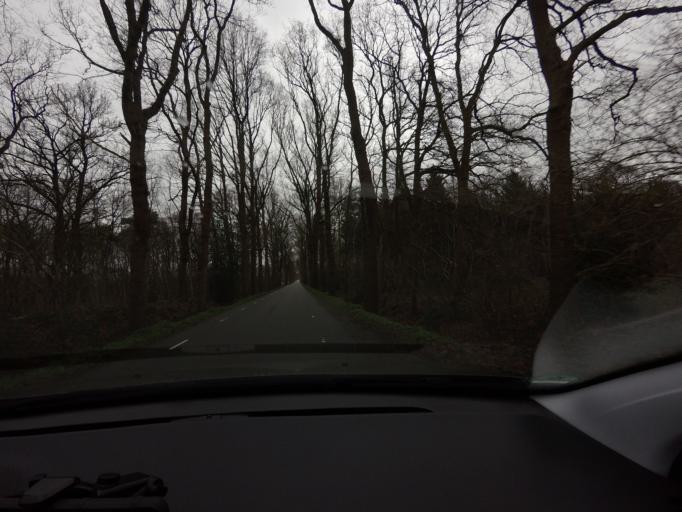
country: NL
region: Drenthe
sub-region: Gemeente Hoogeveen
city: Hoogeveen
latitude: 52.7679
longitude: 6.4933
